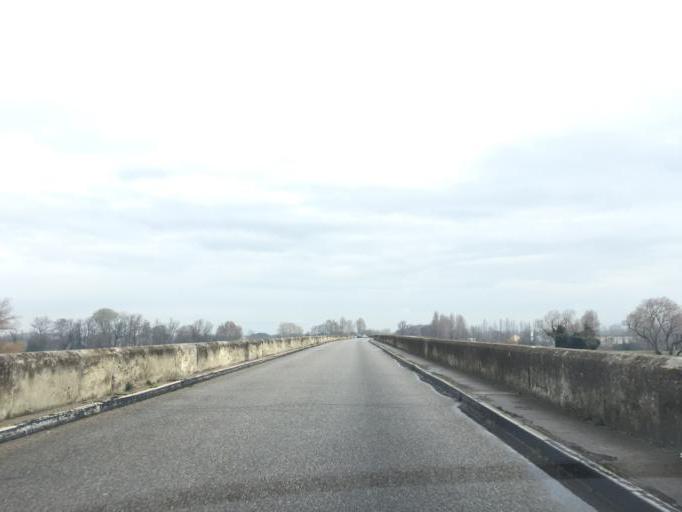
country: FR
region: Languedoc-Roussillon
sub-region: Departement du Gard
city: Pont-Saint-Esprit
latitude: 44.2595
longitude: 4.6529
